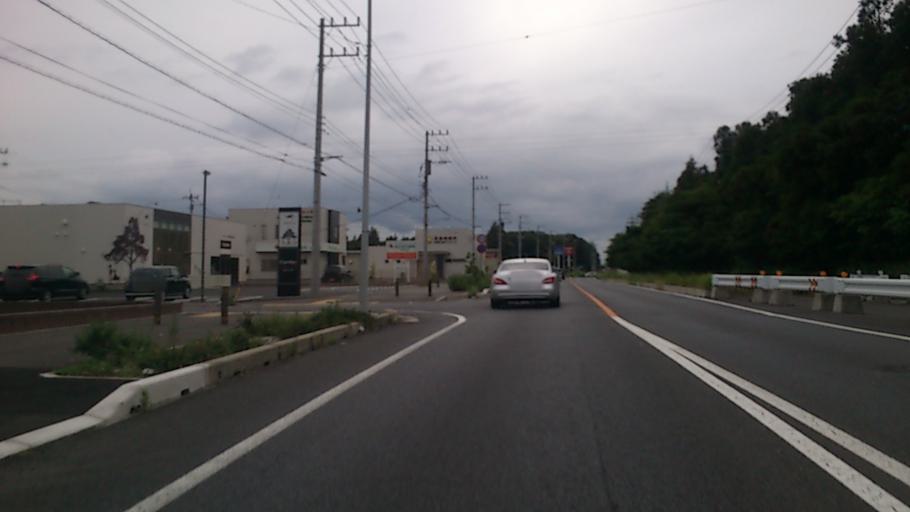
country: JP
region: Ibaraki
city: Naka
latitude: 36.1006
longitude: 140.0800
